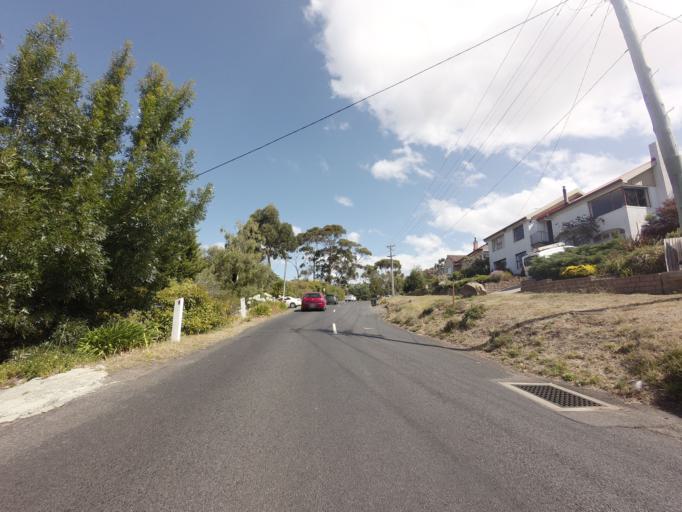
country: AU
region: Tasmania
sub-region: Hobart
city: Dynnyrne
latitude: -42.9188
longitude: 147.3240
